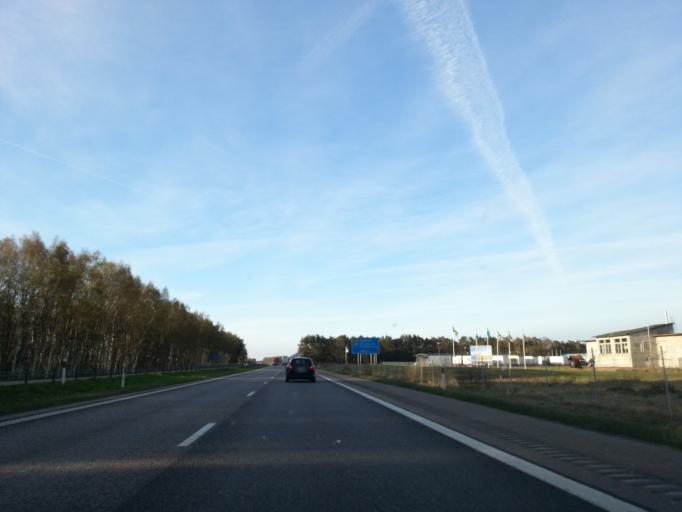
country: SE
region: Halland
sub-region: Laholms Kommun
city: Mellbystrand
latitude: 56.4936
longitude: 12.9553
